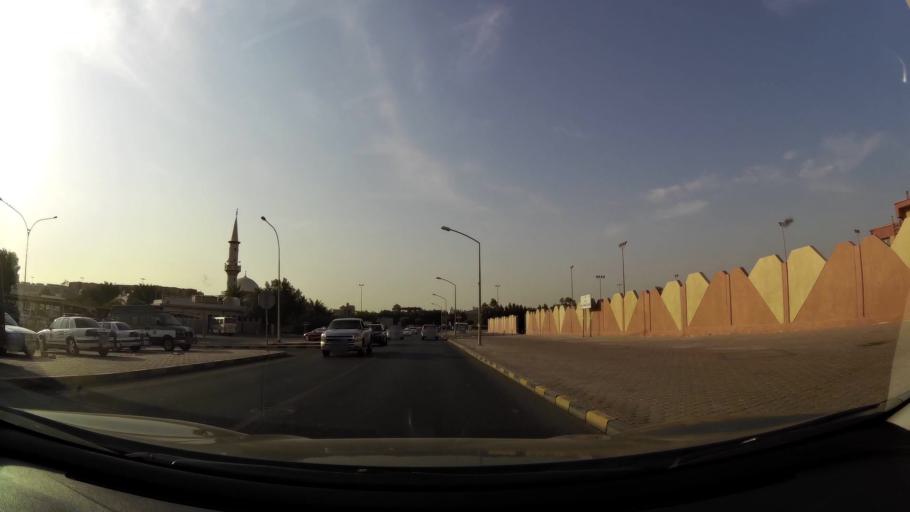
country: KW
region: Muhafazat Hawalli
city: Ar Rumaythiyah
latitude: 29.3176
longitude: 48.0765
